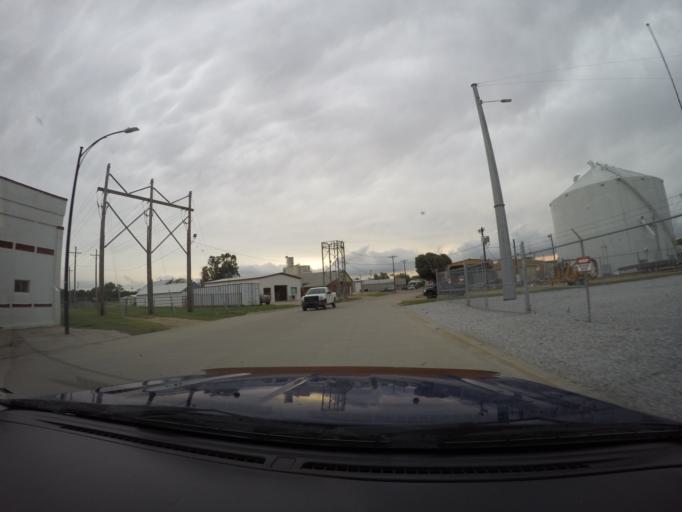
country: US
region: Kansas
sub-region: Clay County
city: Clay Center
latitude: 39.3743
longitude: -97.1282
